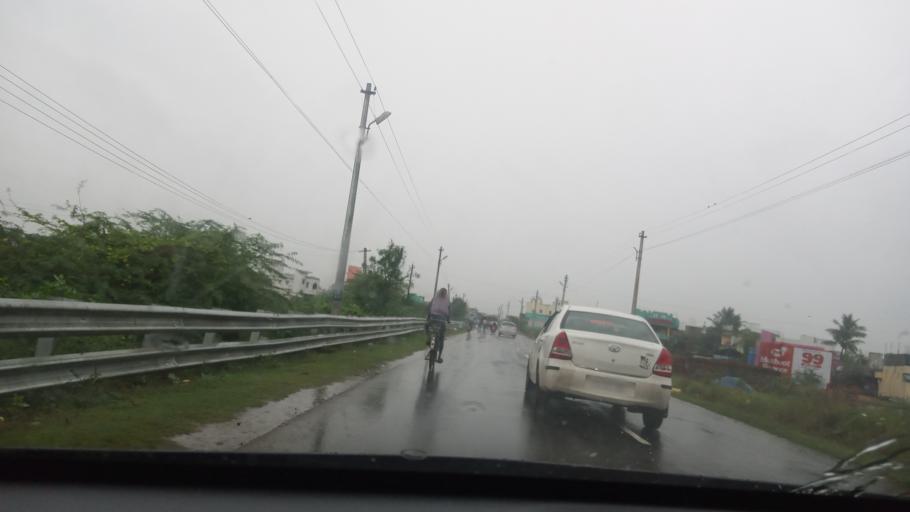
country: IN
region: Tamil Nadu
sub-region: Tiruvannamalai
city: Cheyyar
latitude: 12.6592
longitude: 79.5372
